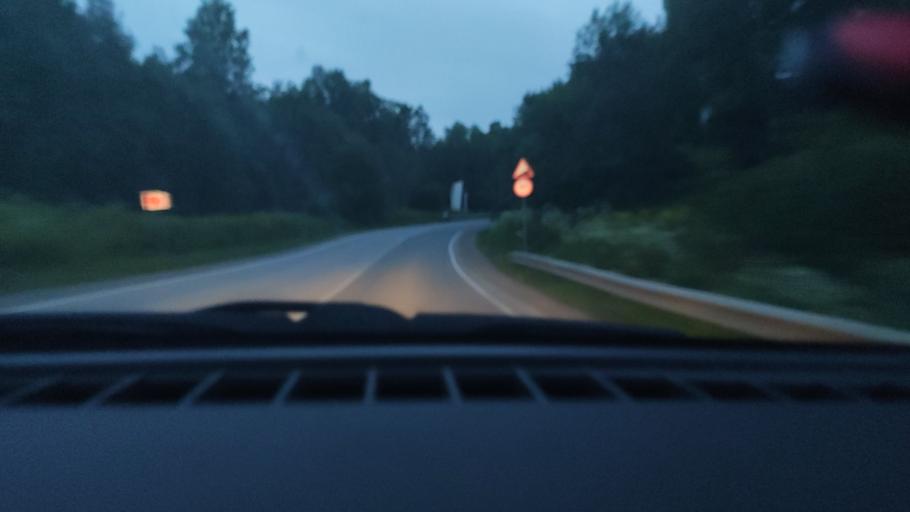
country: RU
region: Perm
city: Zvezdnyy
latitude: 57.7375
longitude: 56.3338
